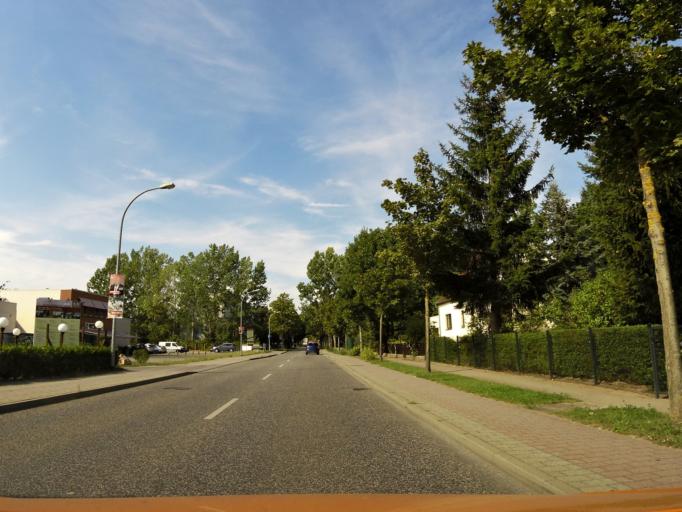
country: DE
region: Brandenburg
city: Teltow
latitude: 52.3930
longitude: 13.2452
